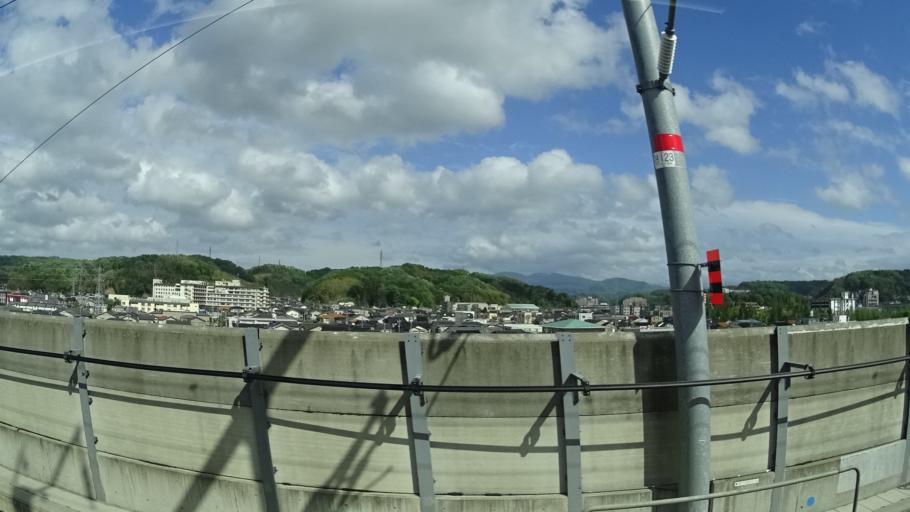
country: JP
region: Ishikawa
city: Kanazawa-shi
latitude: 36.5931
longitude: 136.6715
